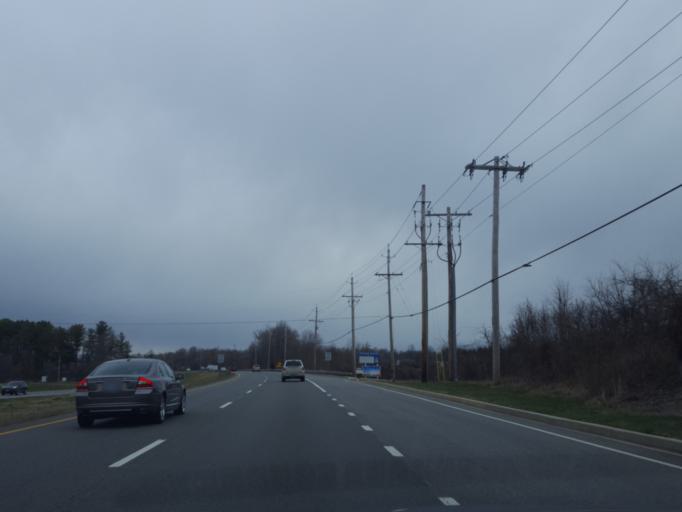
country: US
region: Maryland
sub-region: Calvert County
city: Dunkirk
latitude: 38.7327
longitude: -76.6587
